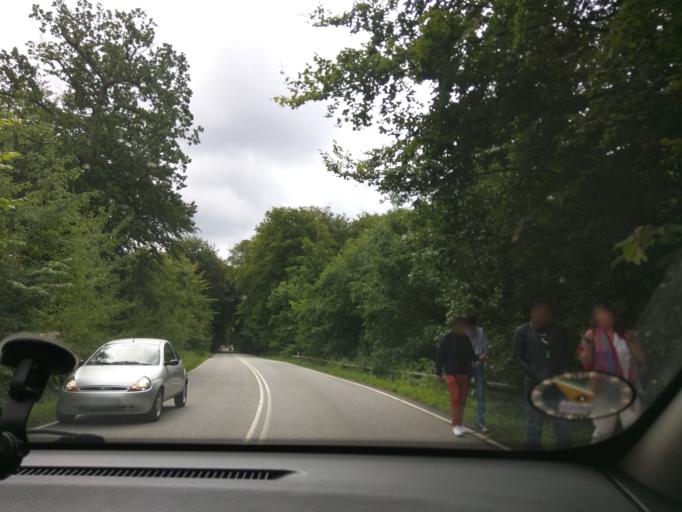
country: DK
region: Zealand
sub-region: Holbaek Kommune
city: Jyderup
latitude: 55.6639
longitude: 11.3916
